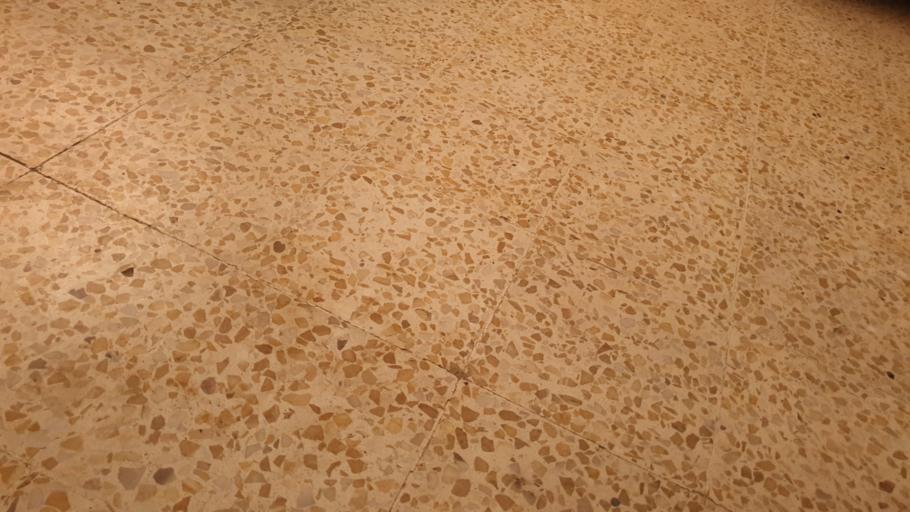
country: IQ
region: Al Muthanna
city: Ar Rumaythah
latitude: 31.5329
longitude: 45.1614
